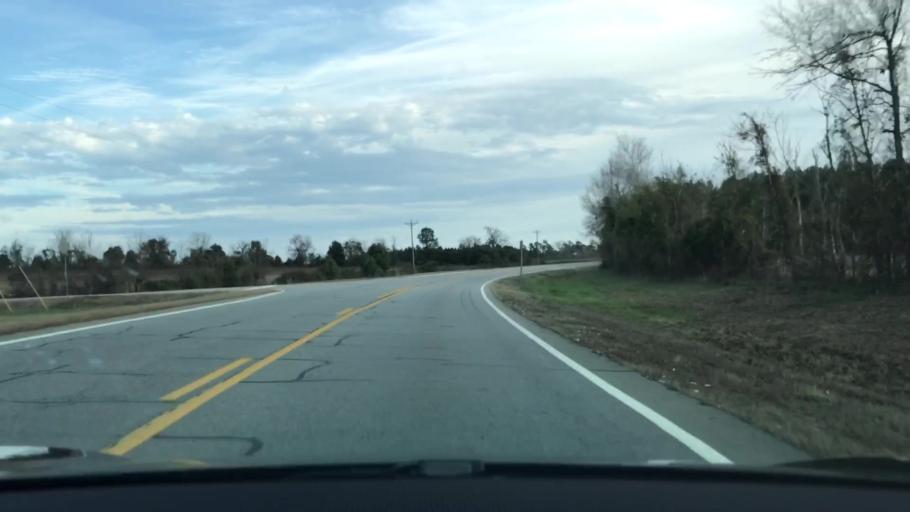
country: US
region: Georgia
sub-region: Glascock County
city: Gibson
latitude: 33.3316
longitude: -82.5624
